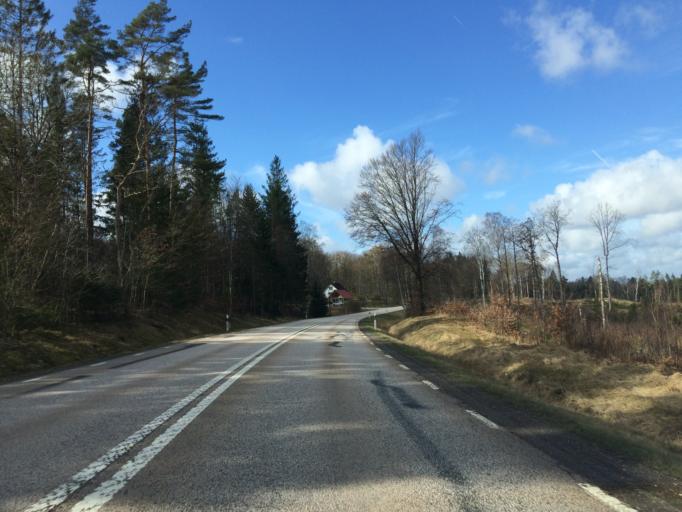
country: SE
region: Kronoberg
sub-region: Markaryds Kommun
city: Markaryd
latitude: 56.4764
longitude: 13.4922
